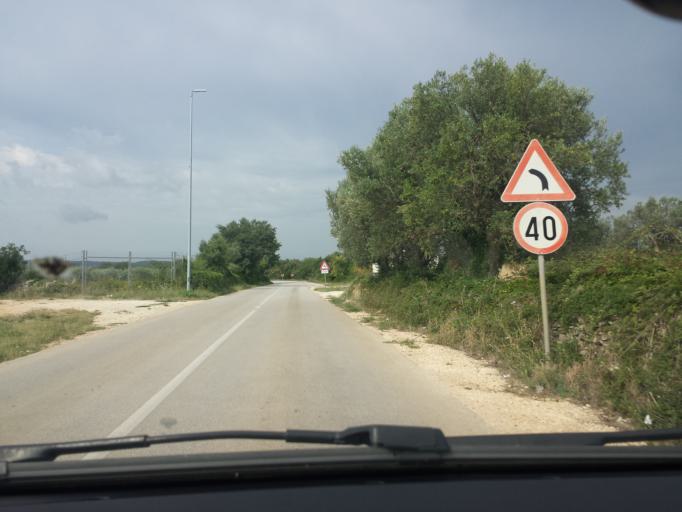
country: HR
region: Istarska
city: Galizana
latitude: 44.9240
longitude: 13.8630
